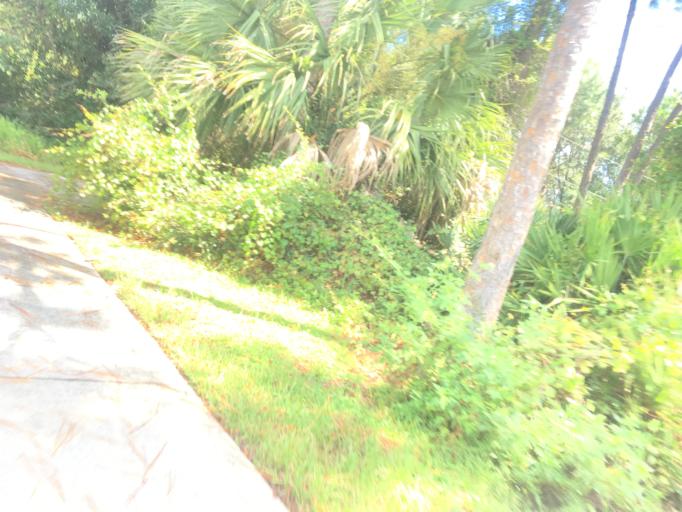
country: US
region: Florida
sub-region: Martin County
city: Palm City
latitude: 27.1790
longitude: -80.2733
